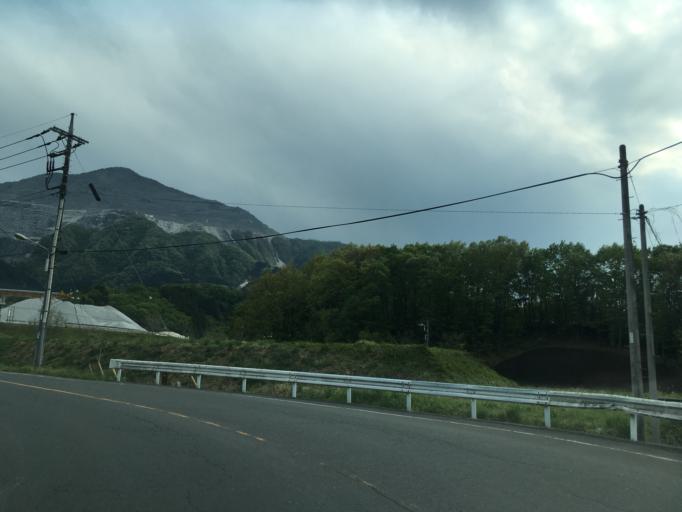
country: JP
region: Saitama
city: Chichibu
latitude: 35.9805
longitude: 139.1009
